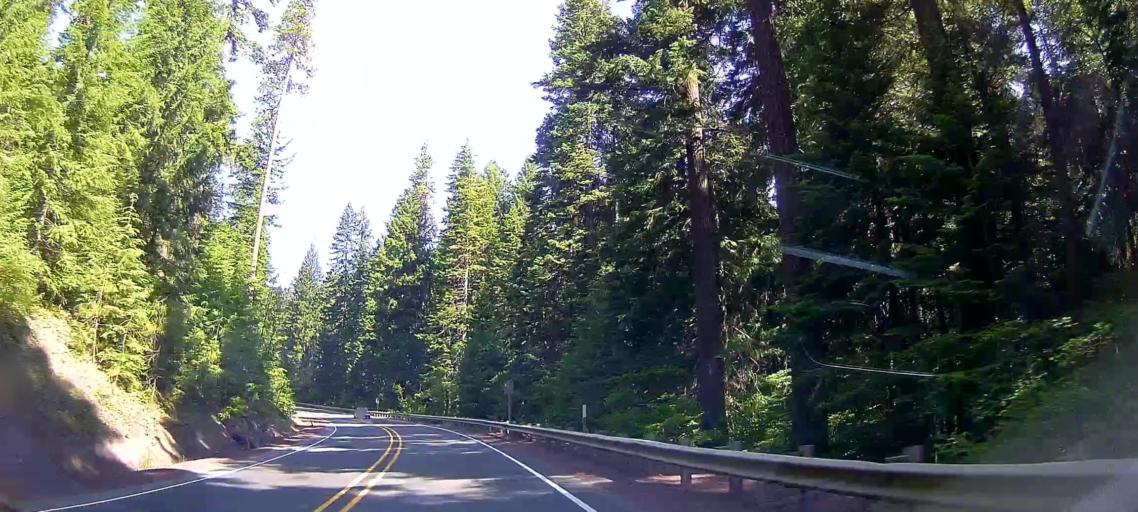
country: US
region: Oregon
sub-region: Jefferson County
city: Warm Springs
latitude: 45.1022
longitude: -121.5522
